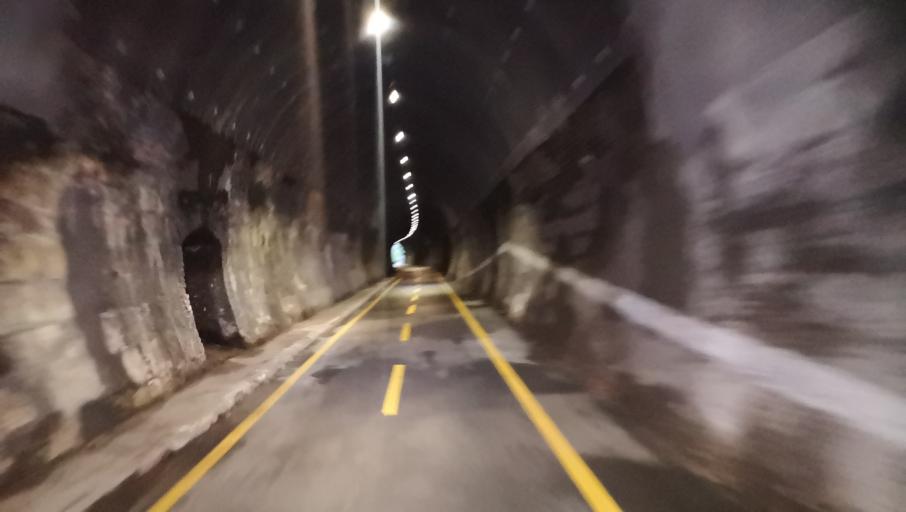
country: IT
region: Friuli Venezia Giulia
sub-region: Provincia di Udine
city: Chiusaforte
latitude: 46.3962
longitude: 13.2667
